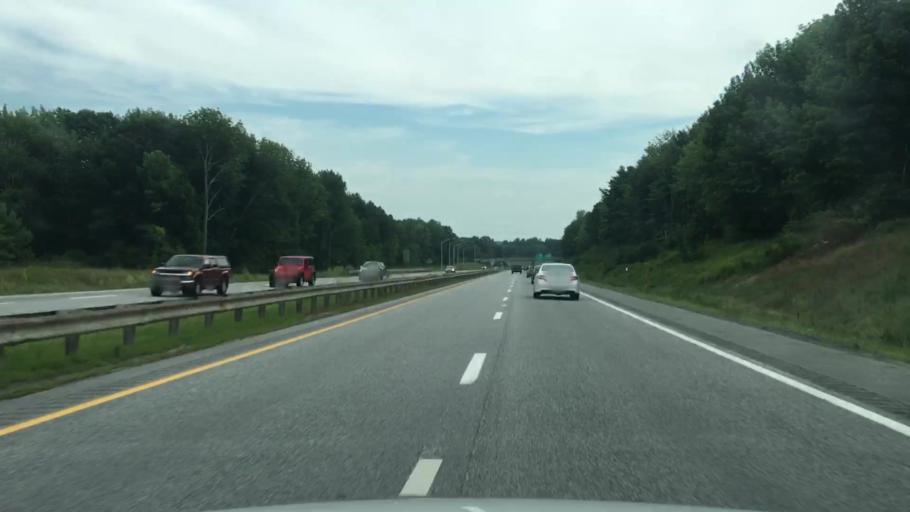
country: US
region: Maine
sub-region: Cumberland County
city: Falmouth
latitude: 43.7400
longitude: -70.3025
